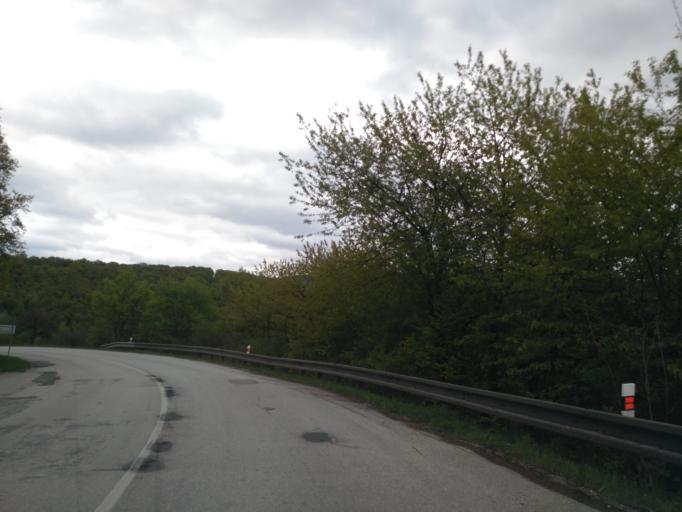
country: SK
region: Kosicky
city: Roznava
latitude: 48.6341
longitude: 20.3591
